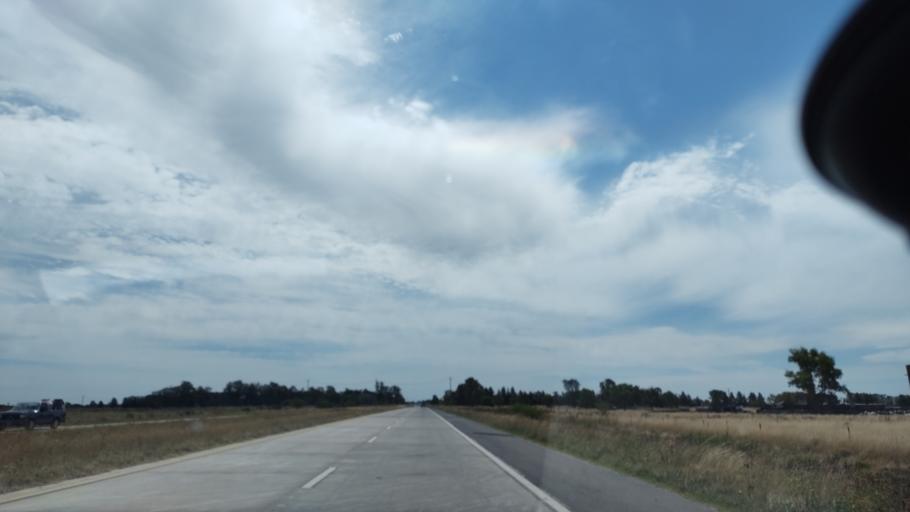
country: AR
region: Buenos Aires
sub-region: Partido de Brandsen
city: Brandsen
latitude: -35.0415
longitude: -58.1758
